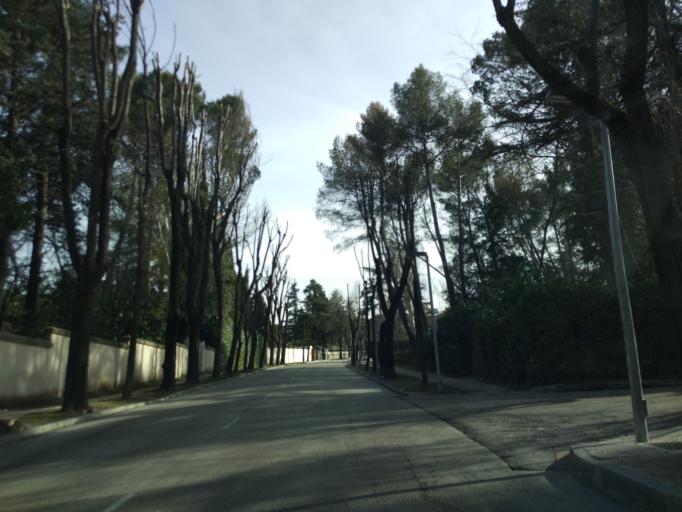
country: ES
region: Madrid
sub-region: Provincia de Madrid
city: Tetuan de las Victorias
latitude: 40.4690
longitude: -3.7314
